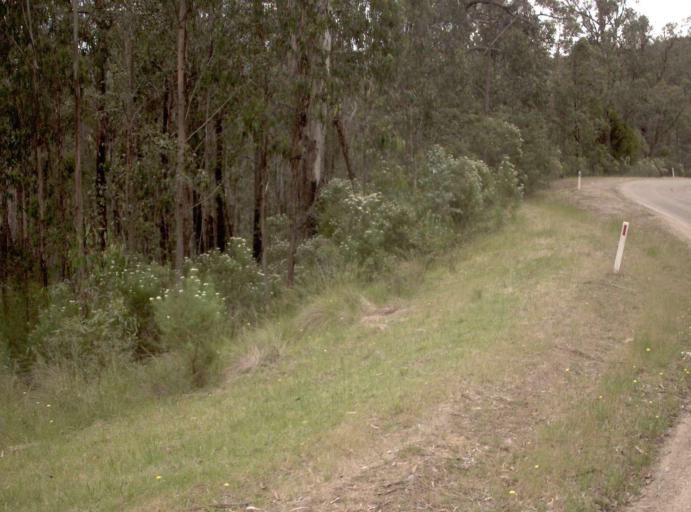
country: AU
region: Victoria
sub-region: East Gippsland
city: Bairnsdale
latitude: -37.6102
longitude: 147.1909
